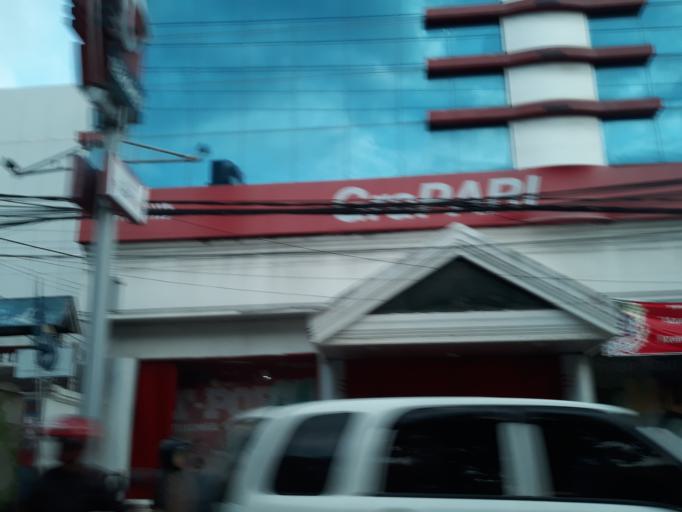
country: ID
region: East Kalimantan
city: Balikpapan
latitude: -1.2704
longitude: 116.8547
